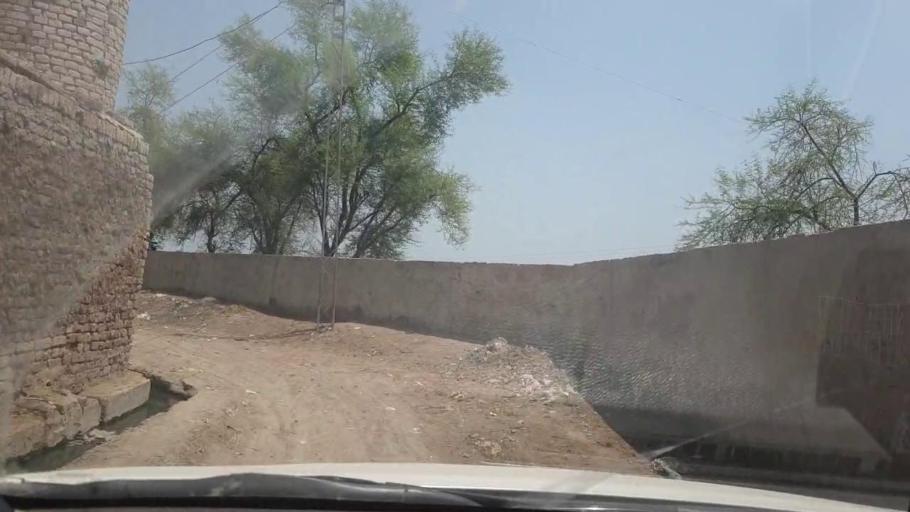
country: PK
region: Sindh
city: Lakhi
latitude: 27.8790
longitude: 68.7287
